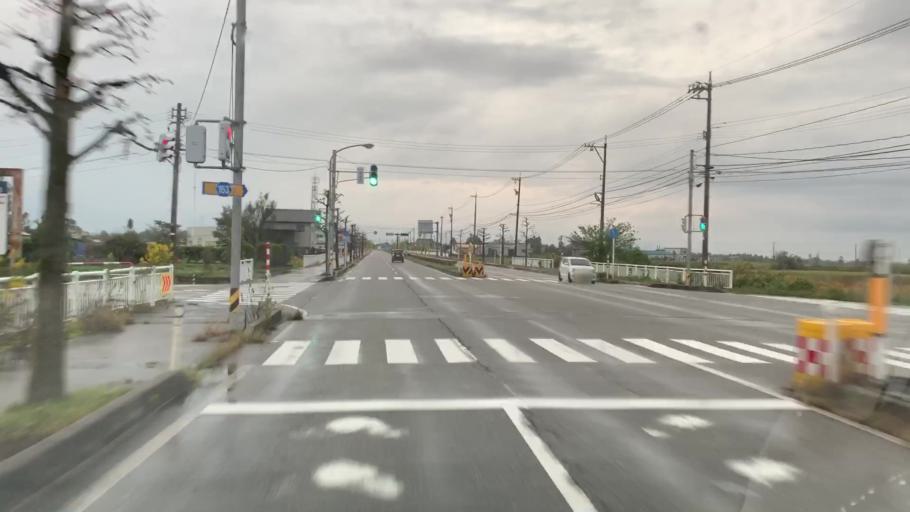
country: JP
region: Toyama
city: Kamiichi
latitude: 36.6914
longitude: 137.3411
